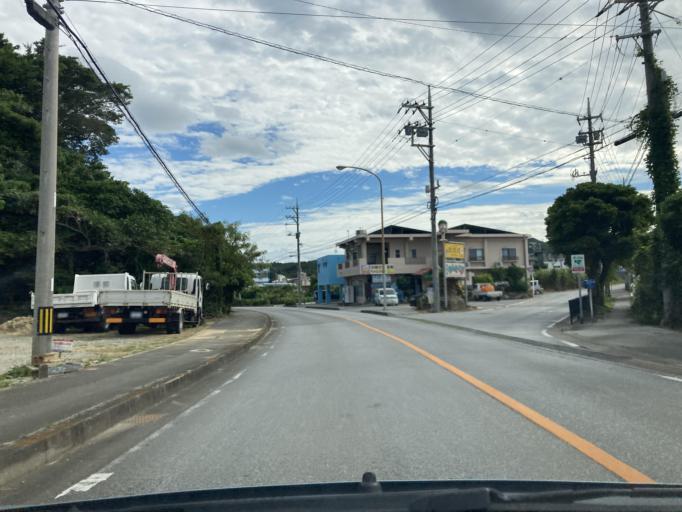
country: JP
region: Okinawa
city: Ishikawa
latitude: 26.4379
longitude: 127.7750
